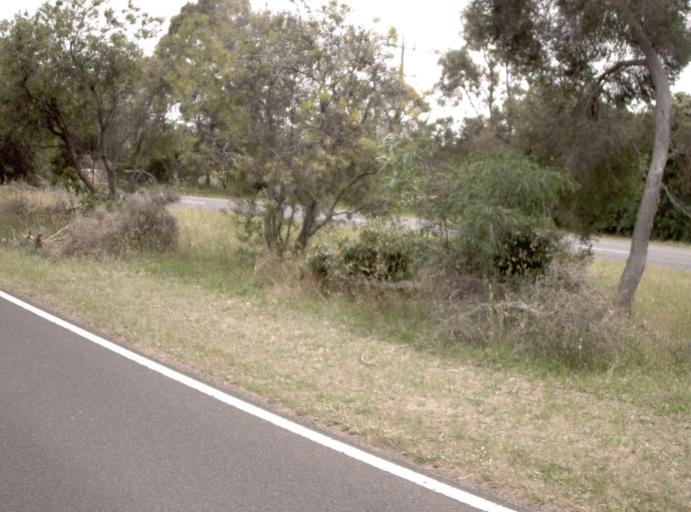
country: AU
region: Victoria
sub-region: Mornington Peninsula
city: Dromana
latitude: -38.3340
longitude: 144.9806
